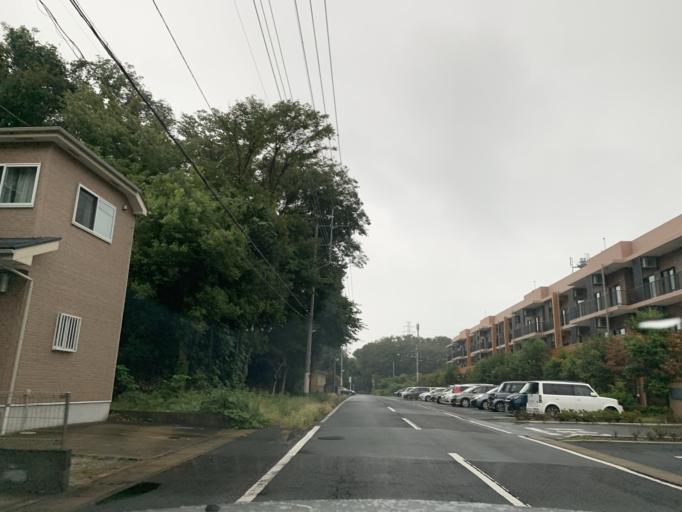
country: JP
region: Chiba
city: Nagareyama
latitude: 35.9097
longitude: 139.9186
